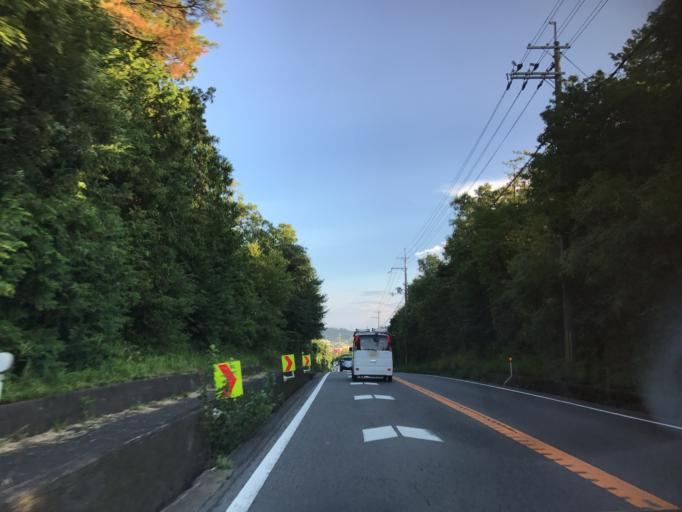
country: JP
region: Shiga Prefecture
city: Hino
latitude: 35.0276
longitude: 136.2396
